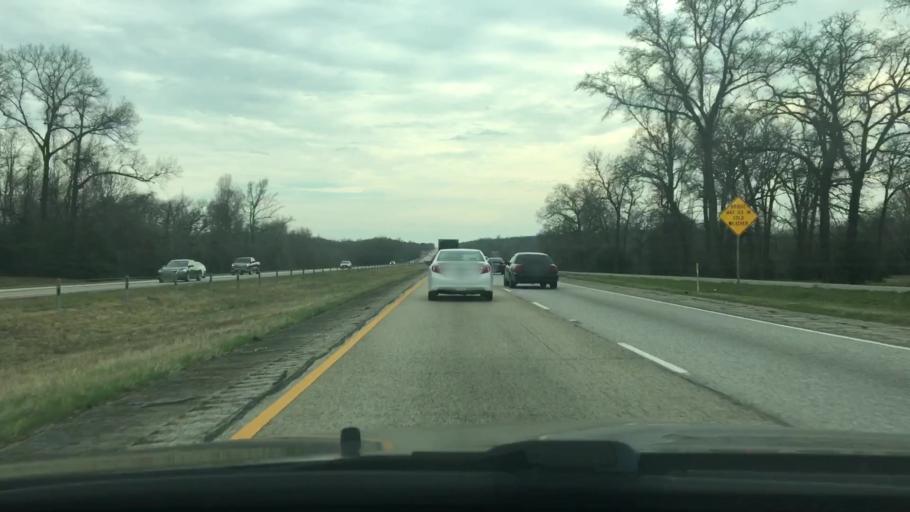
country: US
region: Texas
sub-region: Leon County
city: Centerville
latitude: 31.1935
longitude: -95.9931
